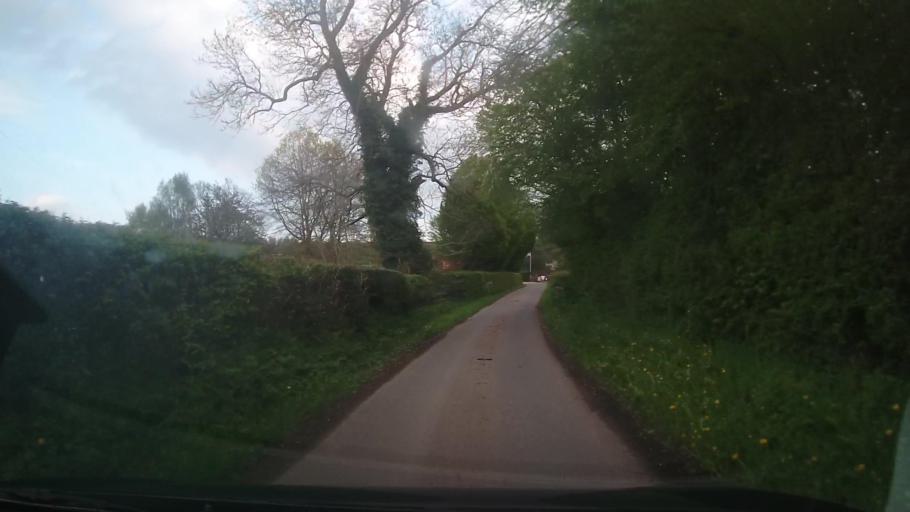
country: GB
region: England
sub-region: Shropshire
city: Ellesmere
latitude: 52.9454
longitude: -2.8694
